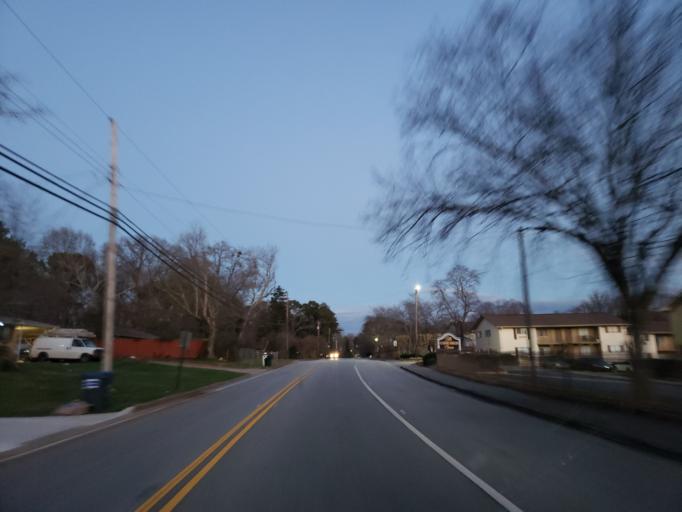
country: US
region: Georgia
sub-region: Cobb County
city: Smyrna
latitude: 33.8677
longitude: -84.5457
